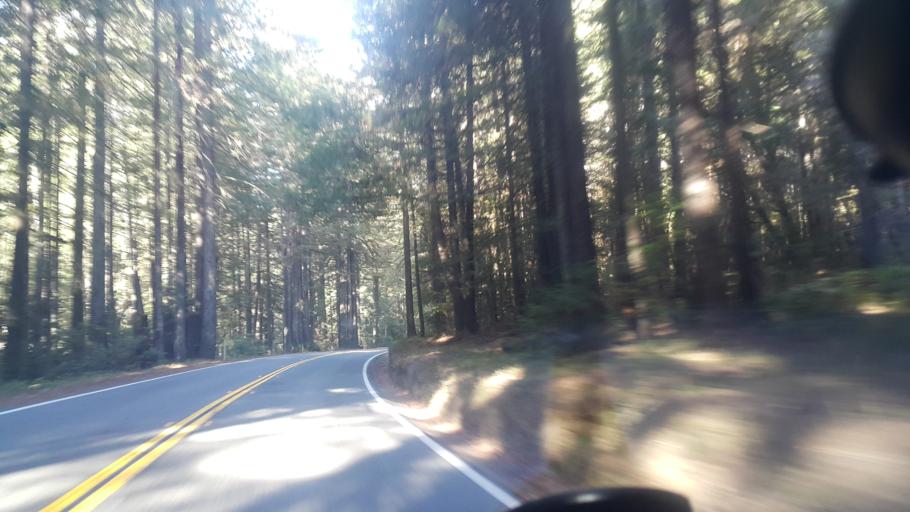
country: US
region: California
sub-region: Mendocino County
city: Brooktrails
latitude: 39.3468
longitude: -123.5362
